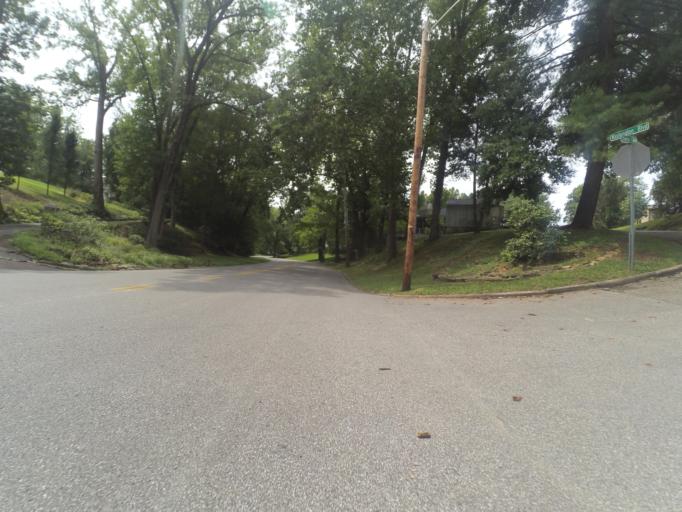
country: US
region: West Virginia
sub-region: Cabell County
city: Huntington
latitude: 38.4044
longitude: -82.4138
